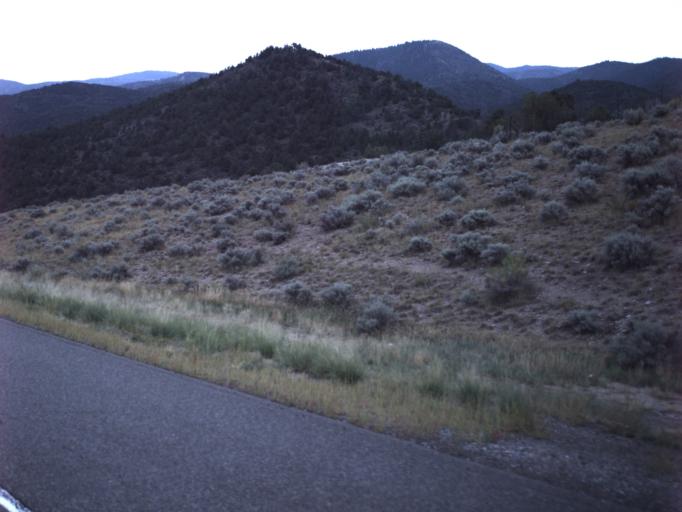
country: US
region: Utah
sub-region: Sevier County
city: Monroe
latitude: 38.5493
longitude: -112.3853
